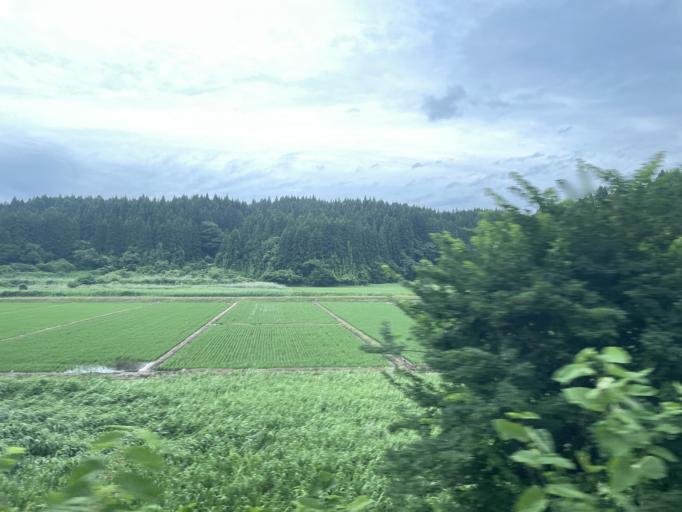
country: JP
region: Akita
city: Tenno
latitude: 39.9142
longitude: 139.8656
